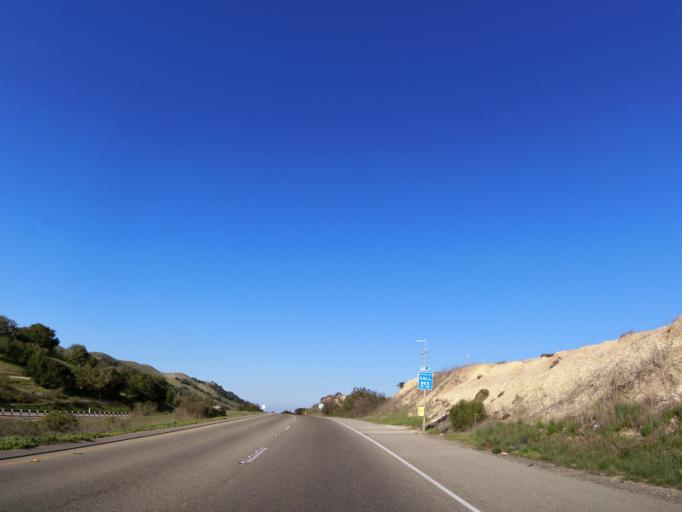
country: US
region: California
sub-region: Santa Barbara County
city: Los Olivos
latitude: 34.7090
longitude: -120.1739
